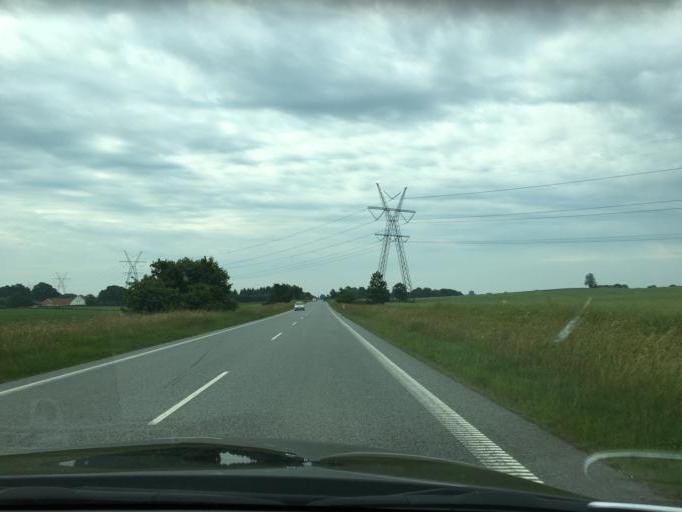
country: DK
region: South Denmark
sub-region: Vejle Kommune
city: Vejle
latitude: 55.6048
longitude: 9.4957
